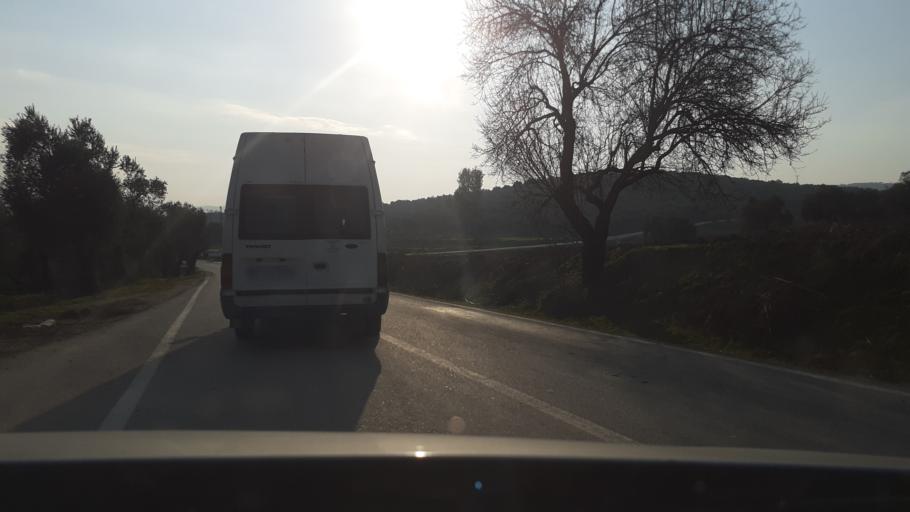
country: TR
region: Hatay
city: Boynuyogun
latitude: 36.1405
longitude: 36.3169
